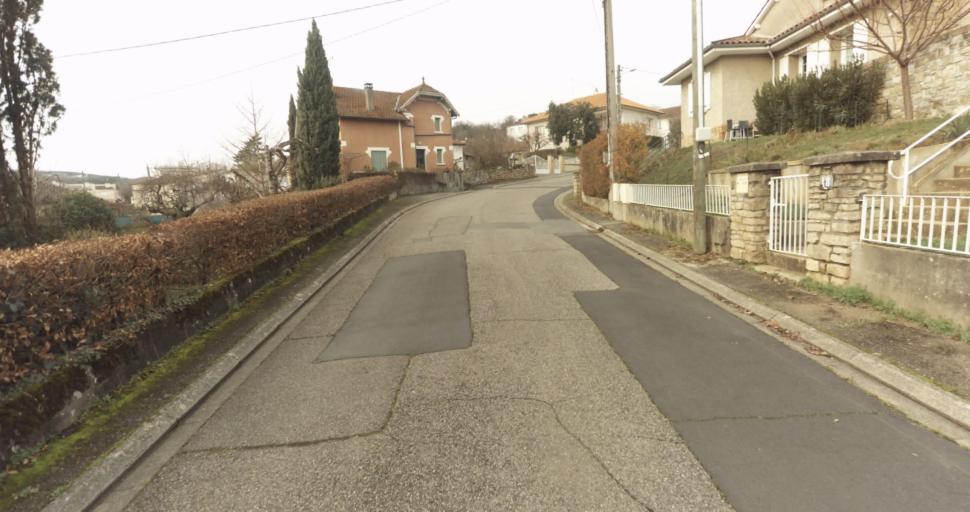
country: FR
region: Midi-Pyrenees
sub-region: Departement du Lot
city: Figeac
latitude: 44.6123
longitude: 2.0249
